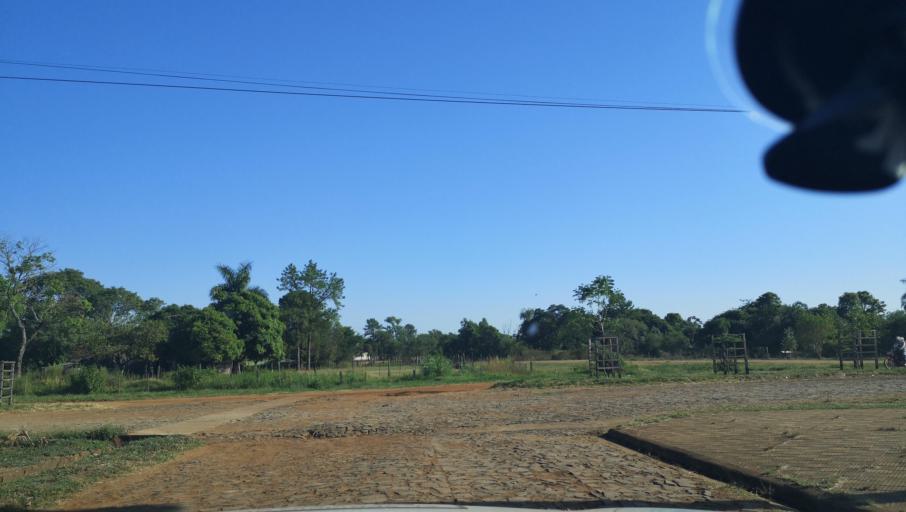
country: PY
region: Itapua
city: Carmen del Parana
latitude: -27.1541
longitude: -56.2408
